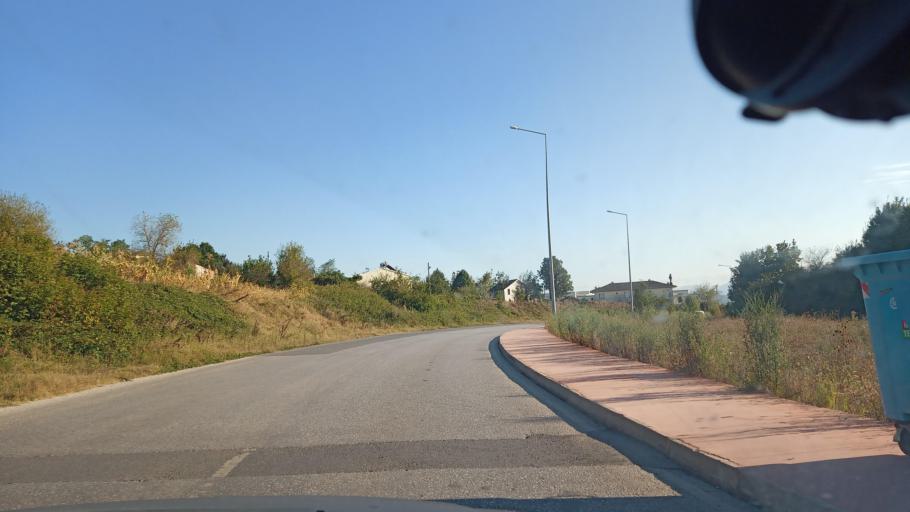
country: TR
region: Sakarya
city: Kazimpasa
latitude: 40.8535
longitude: 30.2799
